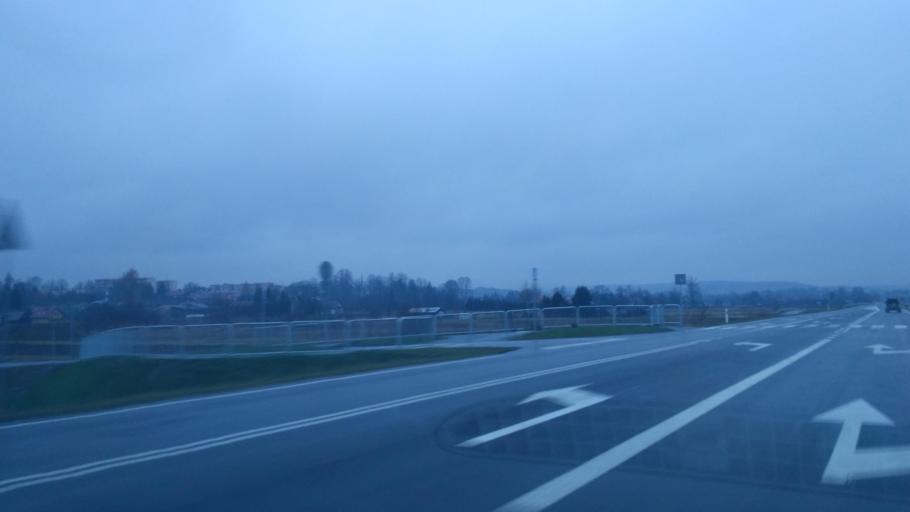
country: PL
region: Subcarpathian Voivodeship
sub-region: Powiat rzeszowski
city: Dynow
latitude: 49.8144
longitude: 22.2406
